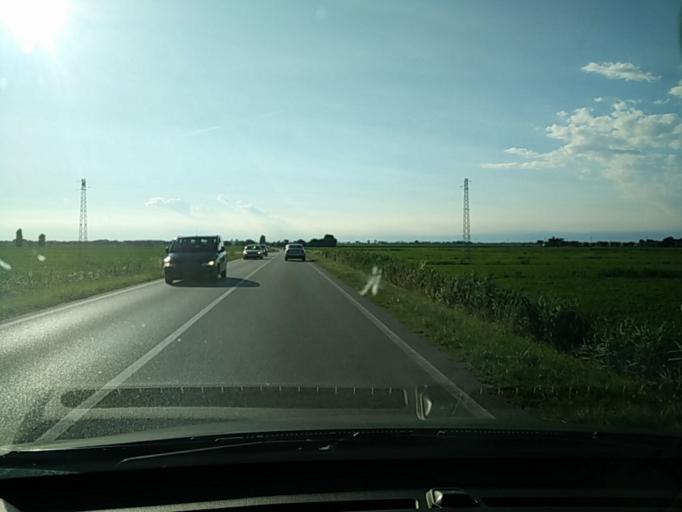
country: IT
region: Veneto
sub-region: Provincia di Venezia
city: Crepaldo
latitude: 45.5637
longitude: 12.7238
